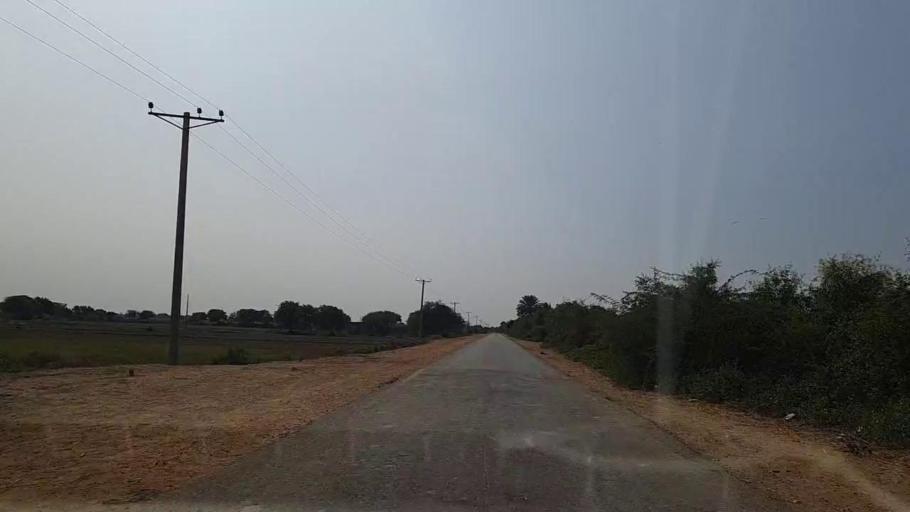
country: PK
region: Sindh
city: Chuhar Jamali
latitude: 24.3529
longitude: 67.9548
